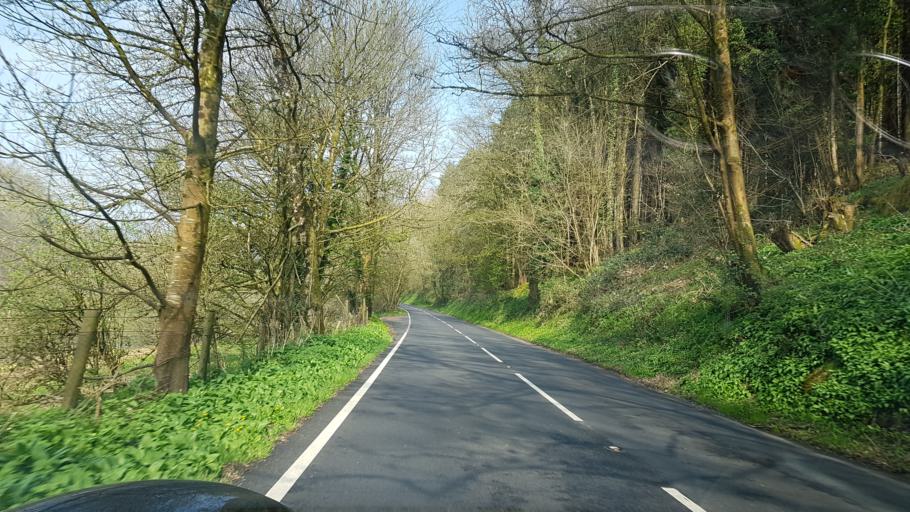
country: GB
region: Wales
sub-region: Monmouthshire
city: Monmouth
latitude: 51.7735
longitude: -2.6769
